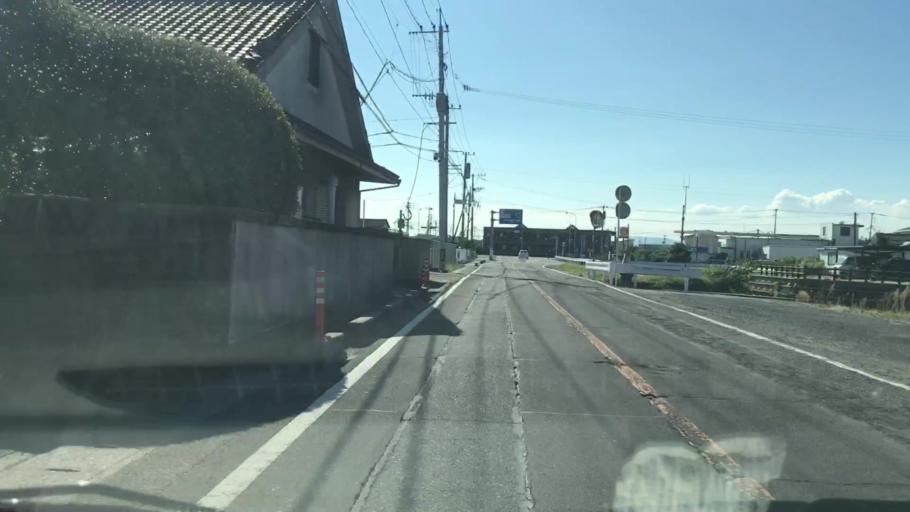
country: JP
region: Saga Prefecture
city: Okawa
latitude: 33.1916
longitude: 130.3174
